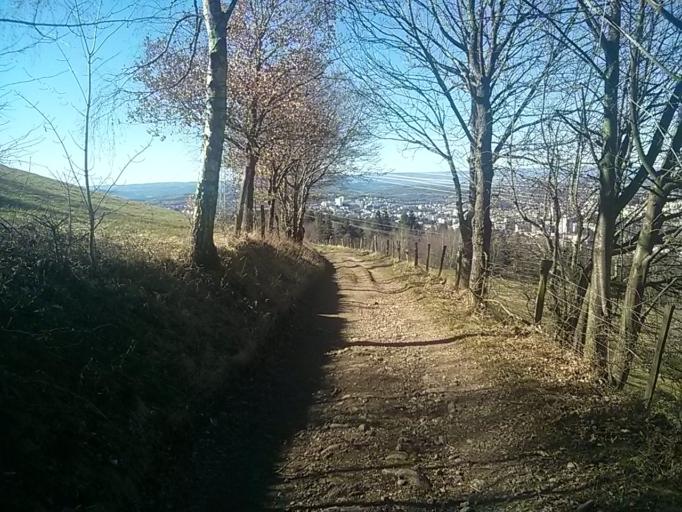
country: FR
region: Rhone-Alpes
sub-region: Departement de la Loire
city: Saint-Jean-Bonnefonds
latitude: 45.4174
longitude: 4.4370
